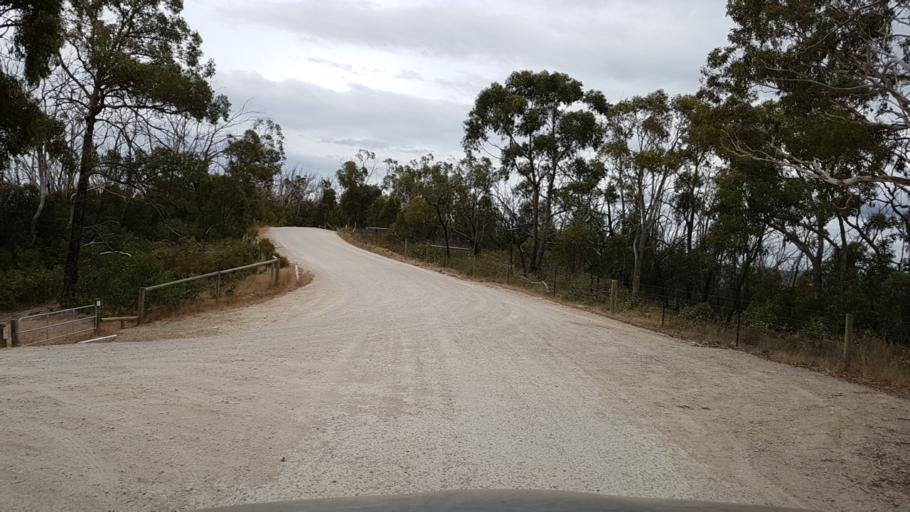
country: AU
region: South Australia
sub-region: Tea Tree Gully
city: Golden Grove
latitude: -34.7752
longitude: 138.8143
